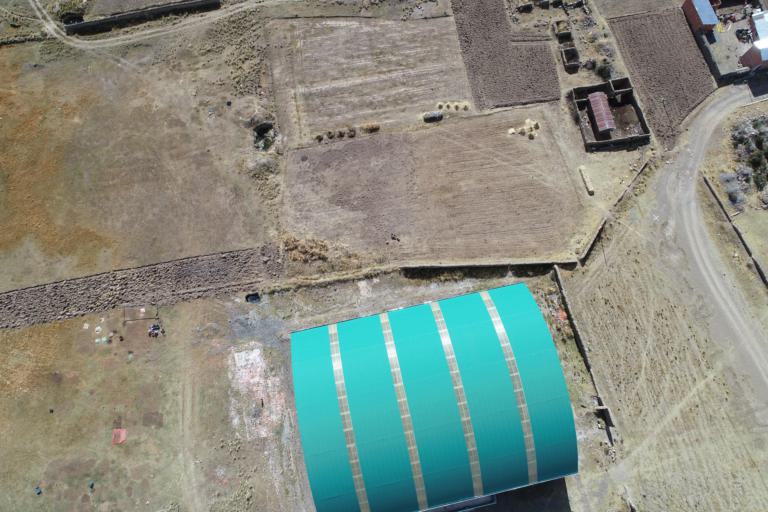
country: BO
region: La Paz
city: Achacachi
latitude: -15.8948
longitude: -68.9093
